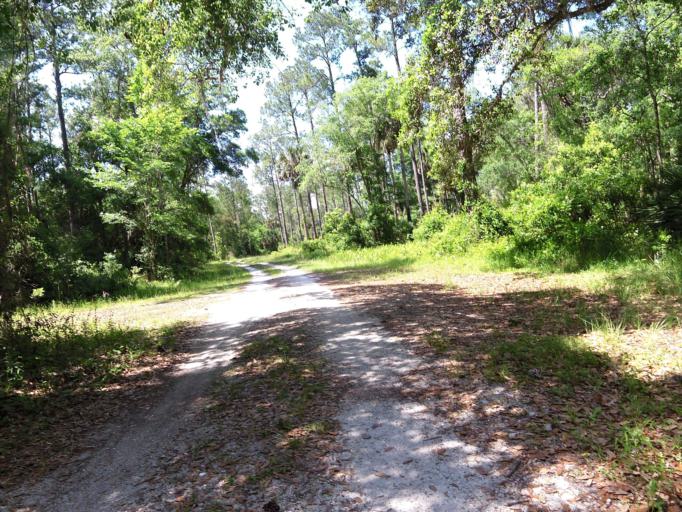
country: US
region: Florida
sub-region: Saint Johns County
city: Palm Valley
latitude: 30.1375
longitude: -81.3773
